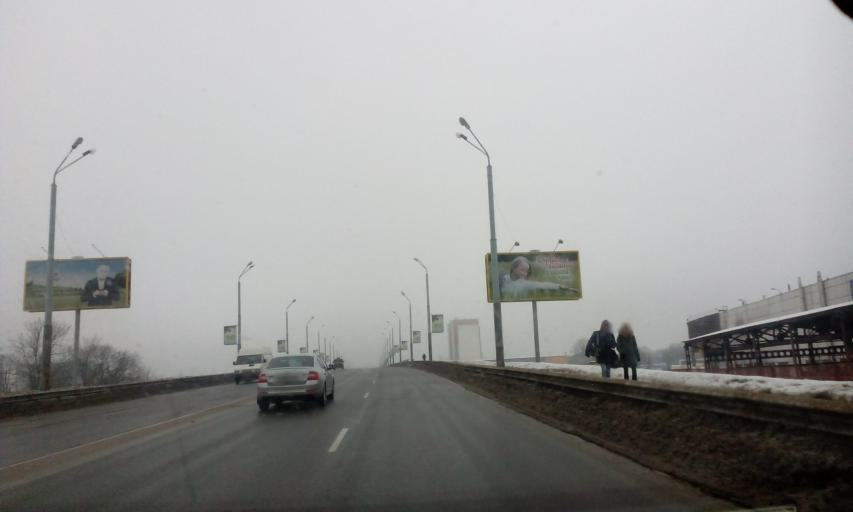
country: BY
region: Mogilev
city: Mahilyow
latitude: 53.9186
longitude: 30.3489
